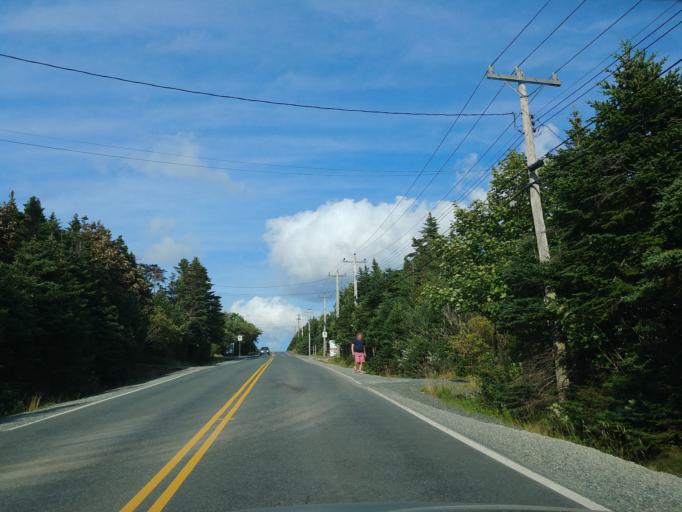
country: CA
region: Newfoundland and Labrador
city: St. John's
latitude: 47.5705
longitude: -52.7598
